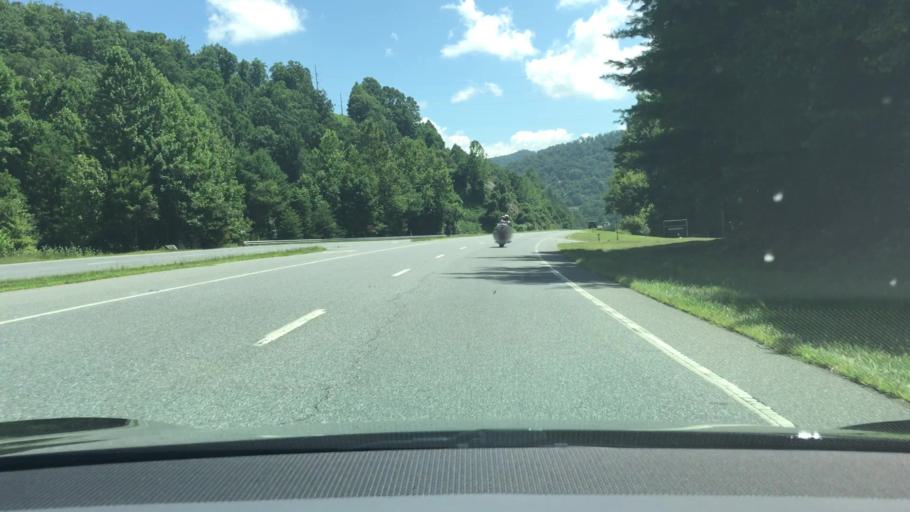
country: US
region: North Carolina
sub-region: Jackson County
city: Sylva
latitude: 35.2918
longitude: -83.2796
